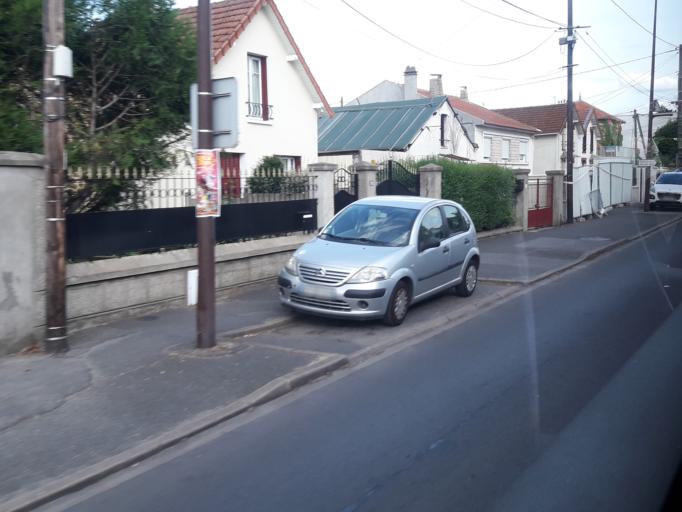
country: FR
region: Ile-de-France
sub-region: Departement de l'Essonne
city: Epinay-sur-Orge
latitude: 48.6777
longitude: 2.3195
